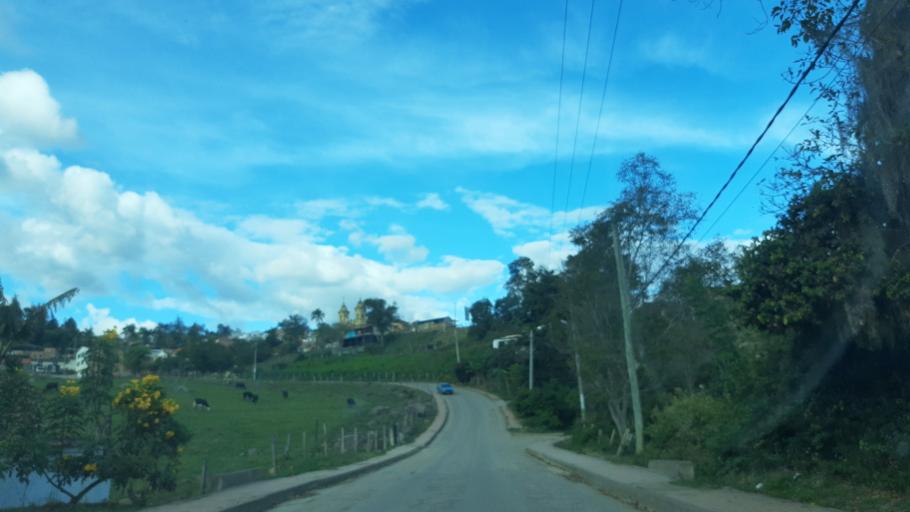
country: CO
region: Cundinamarca
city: Macheta
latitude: 5.0787
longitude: -73.6104
